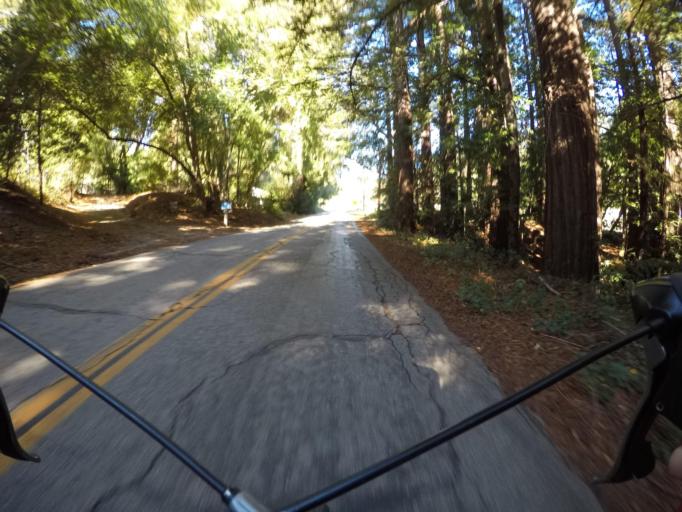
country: US
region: California
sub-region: Santa Clara County
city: Lexington Hills
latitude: 37.1059
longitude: -121.9882
